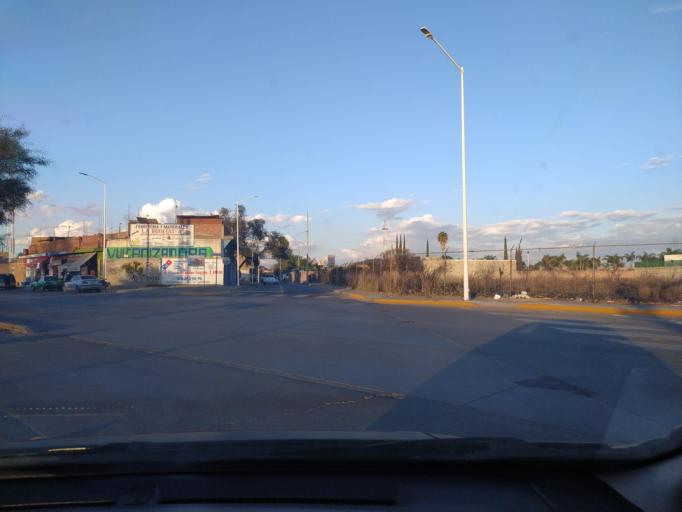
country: LA
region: Oudomxai
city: Muang La
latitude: 21.0079
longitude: 101.8701
